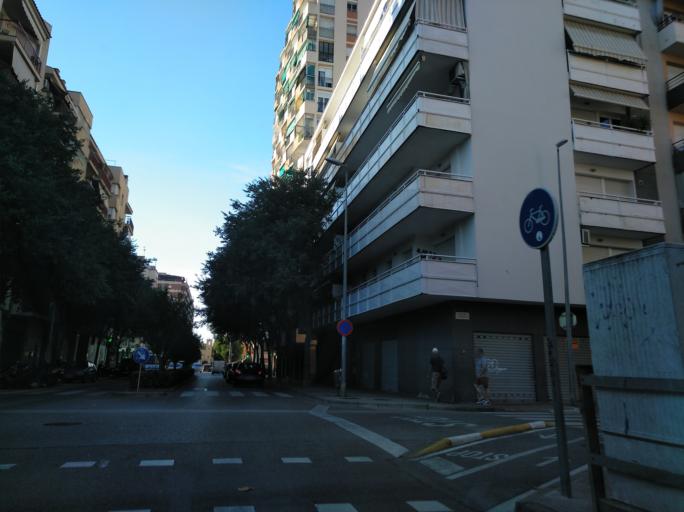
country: ES
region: Catalonia
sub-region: Provincia de Girona
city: Salt
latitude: 41.9719
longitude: 2.7922
